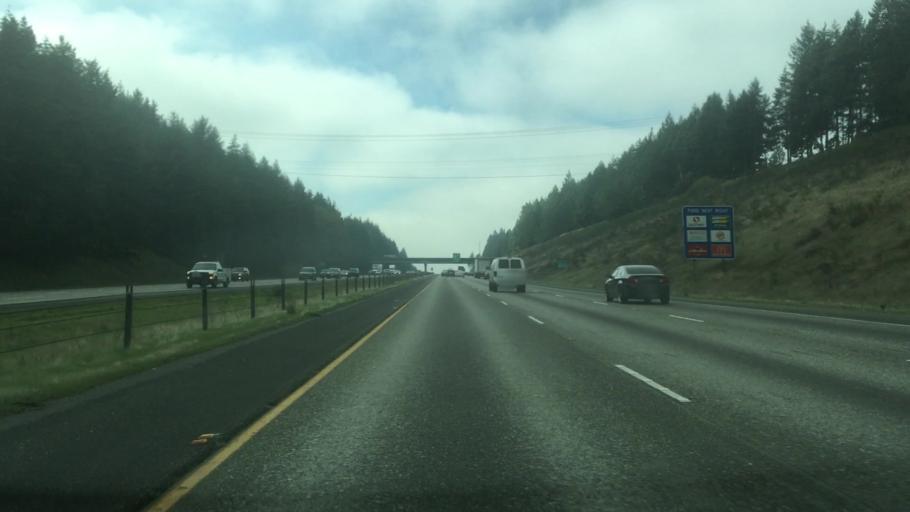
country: US
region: Washington
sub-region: Thurston County
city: Tanglewilde-Thompson Place
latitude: 47.0673
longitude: -122.7361
